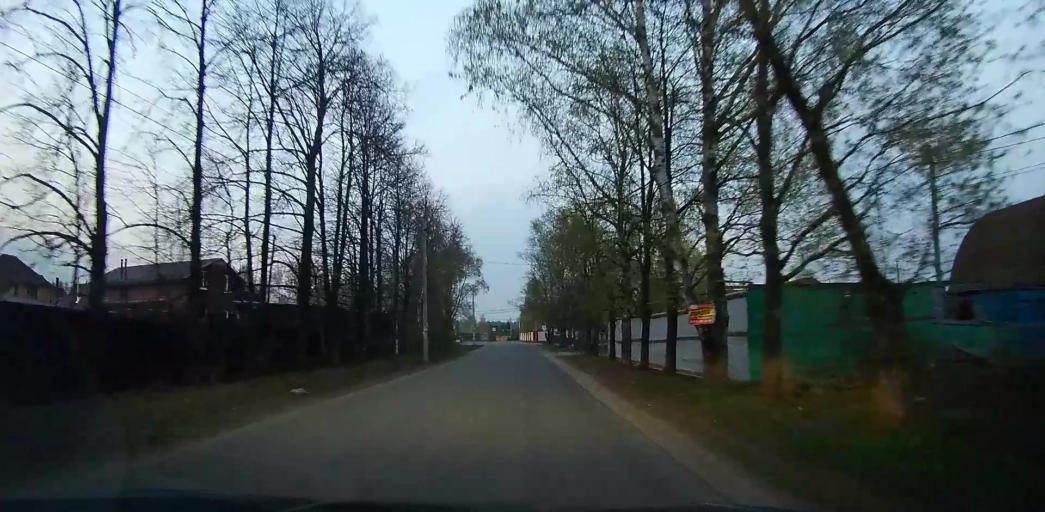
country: RU
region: Moskovskaya
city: Ramenskoye
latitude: 55.5760
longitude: 38.3009
